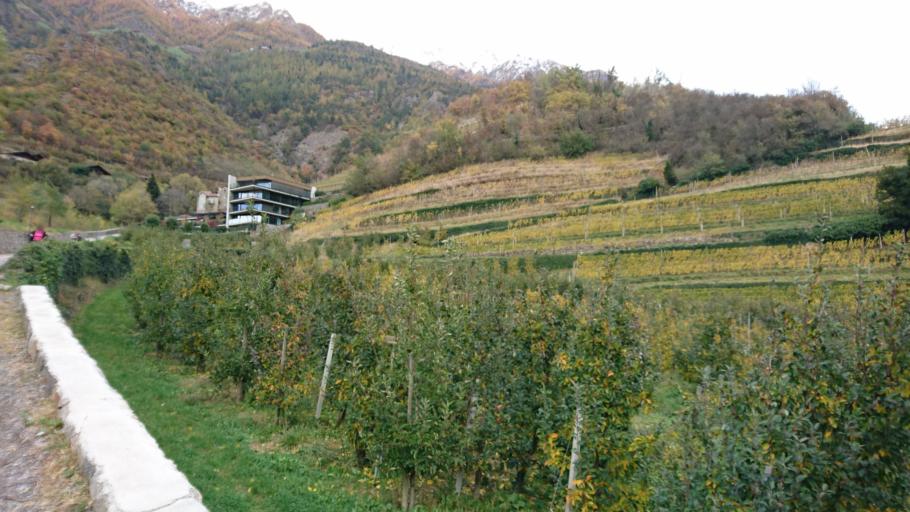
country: IT
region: Trentino-Alto Adige
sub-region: Bolzano
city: Naturno
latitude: 46.6533
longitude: 11.0017
